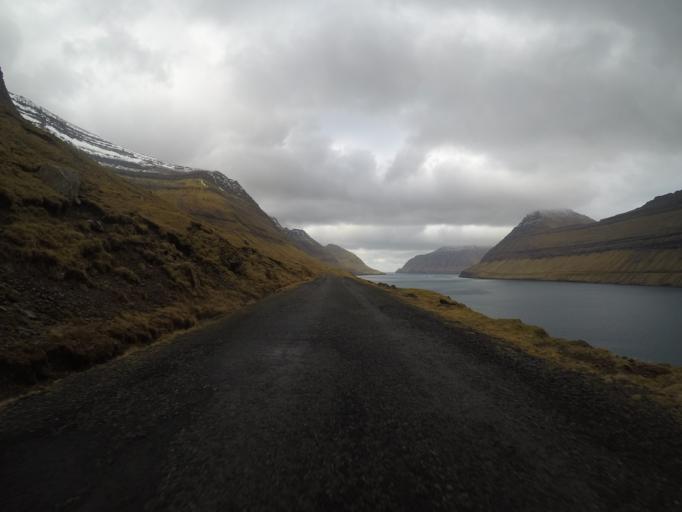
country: FO
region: Nordoyar
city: Klaksvik
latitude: 62.3137
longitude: -6.5514
